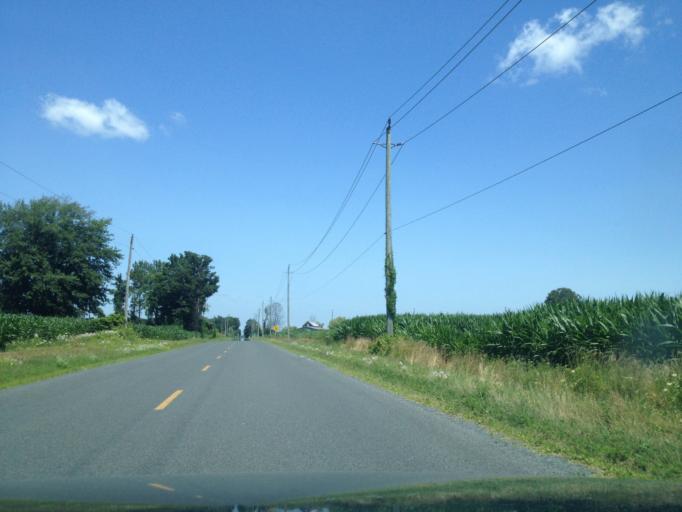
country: CA
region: Ontario
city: Aylmer
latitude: 42.6315
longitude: -80.7208
